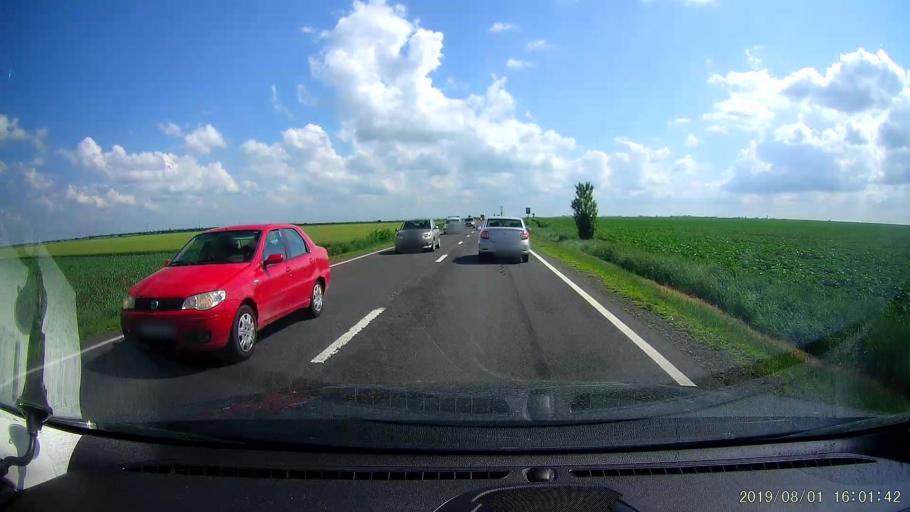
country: RO
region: Ialomita
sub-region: Comuna Ciulnita
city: Ciulnita
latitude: 44.5037
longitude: 27.3895
